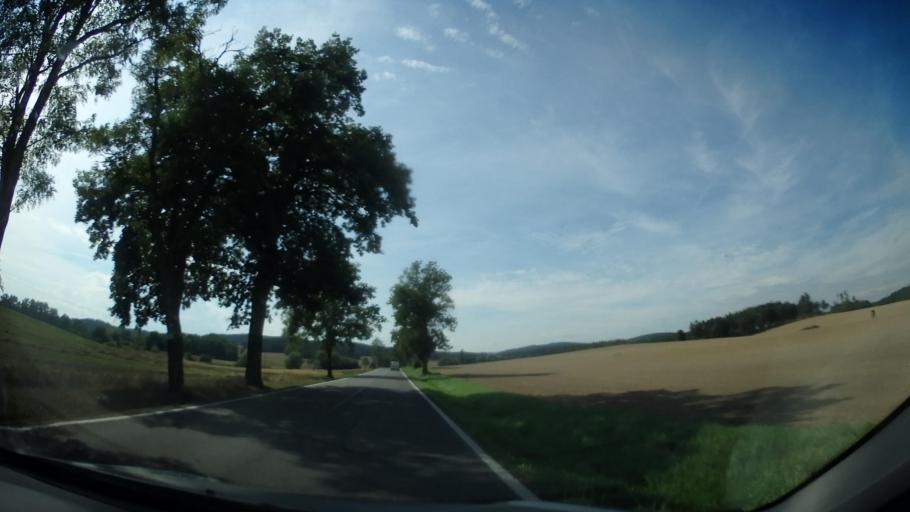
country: CZ
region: Jihocesky
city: Radomysl
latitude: 49.2948
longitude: 14.0335
